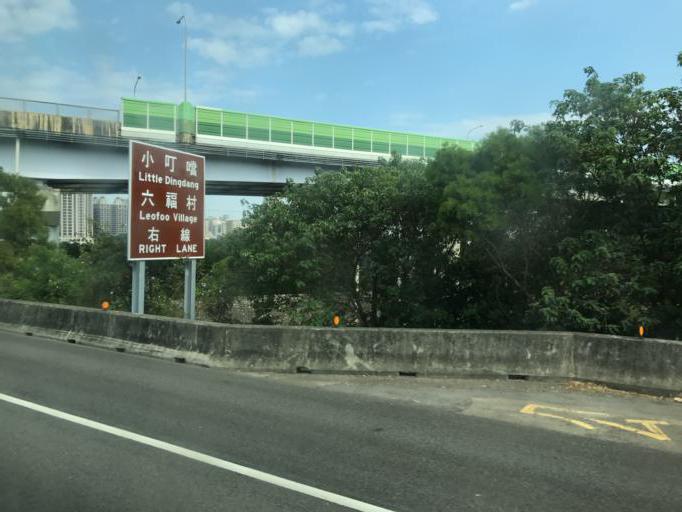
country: TW
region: Taiwan
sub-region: Hsinchu
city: Zhubei
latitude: 24.8096
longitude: 121.0108
